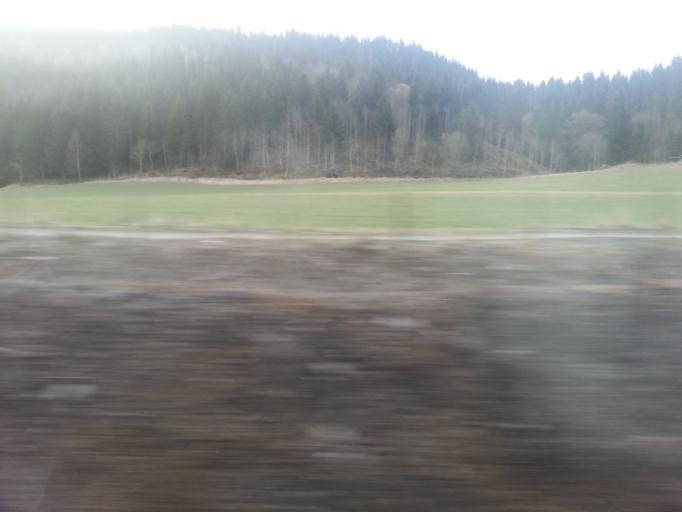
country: NO
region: Sor-Trondelag
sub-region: Melhus
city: Melhus
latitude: 63.2390
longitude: 10.2806
